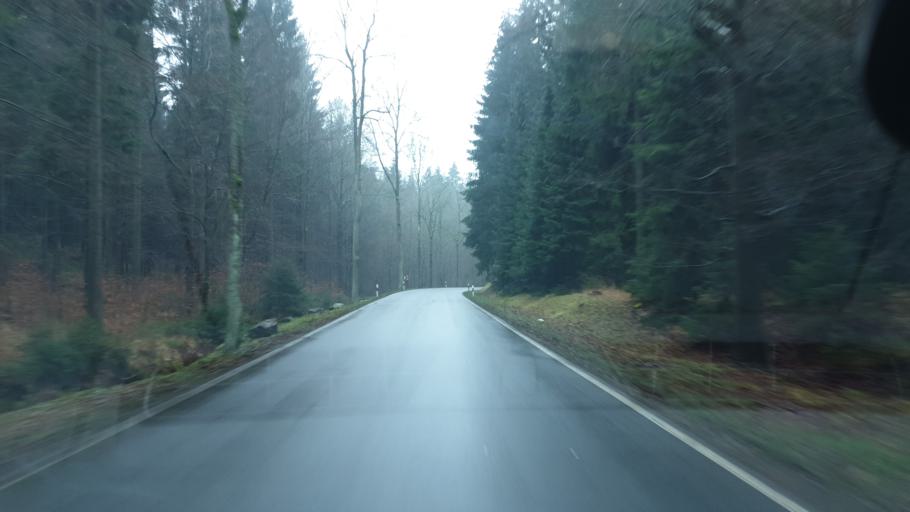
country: DE
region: Saxony
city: Seiffen
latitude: 50.6339
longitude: 13.4200
